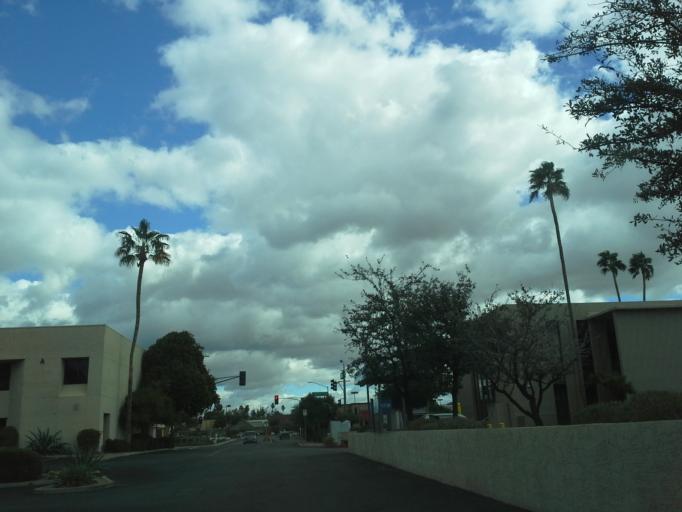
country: US
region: Arizona
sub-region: Maricopa County
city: Paradise Valley
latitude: 33.4766
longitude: -111.9880
